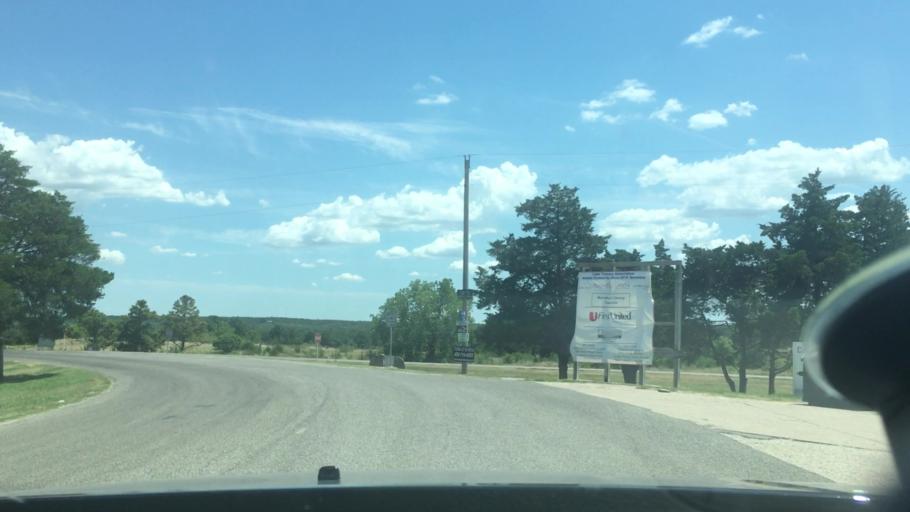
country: US
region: Oklahoma
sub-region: Marshall County
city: Kingston
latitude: 33.9975
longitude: -96.6394
